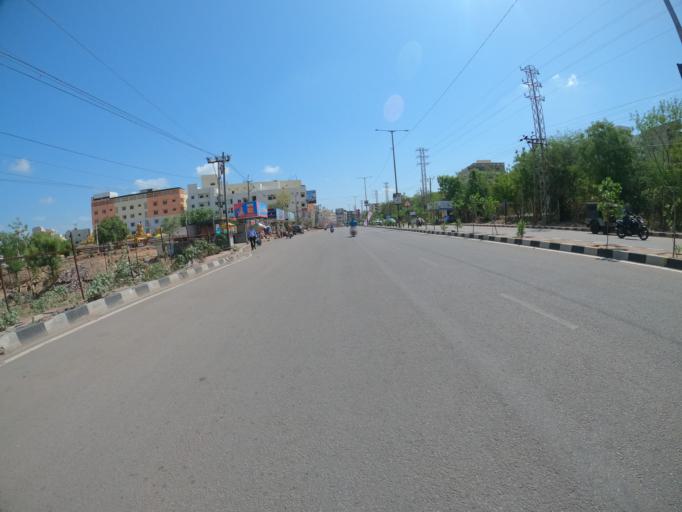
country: IN
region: Telangana
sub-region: Hyderabad
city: Hyderabad
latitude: 17.3625
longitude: 78.3939
